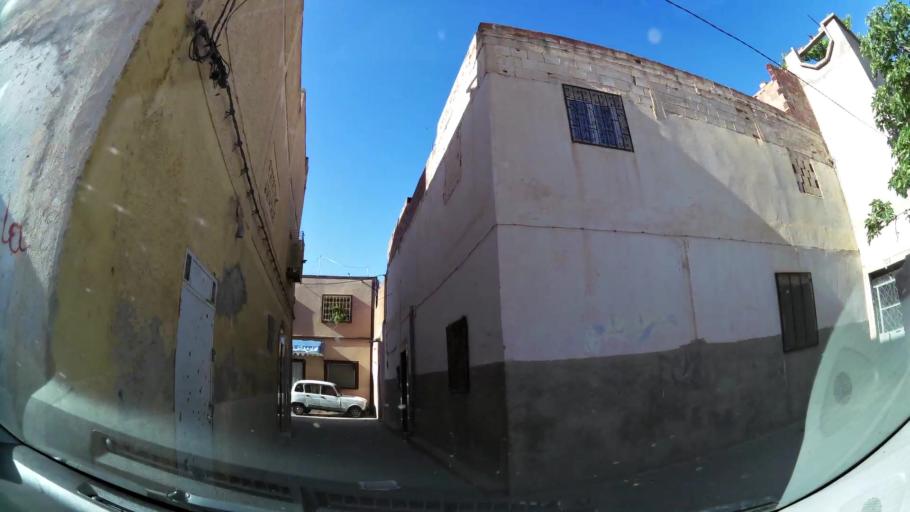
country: MA
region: Oriental
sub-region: Oujda-Angad
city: Oujda
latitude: 34.6801
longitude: -1.9304
